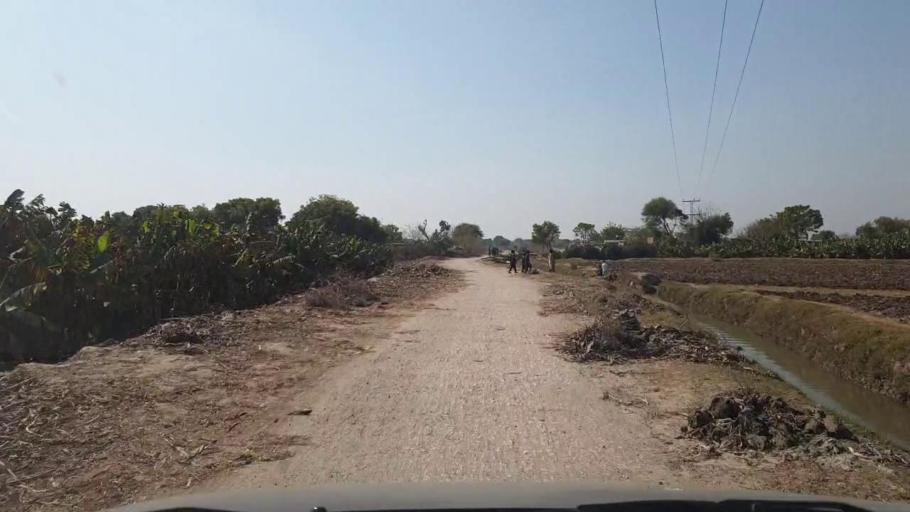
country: PK
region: Sindh
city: Tando Jam
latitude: 25.4248
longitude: 68.6308
